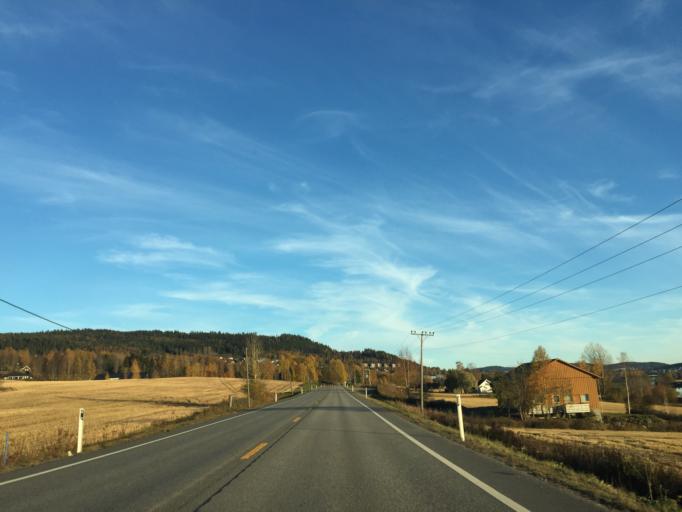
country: NO
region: Hedmark
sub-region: Kongsvinger
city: Kongsvinger
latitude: 60.2134
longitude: 11.9498
